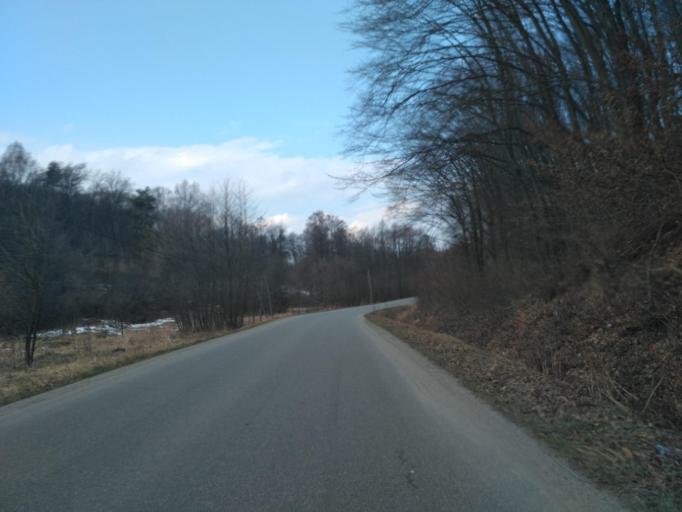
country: PL
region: Subcarpathian Voivodeship
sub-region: Powiat brzozowski
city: Gorki
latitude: 49.6360
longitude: 22.0562
